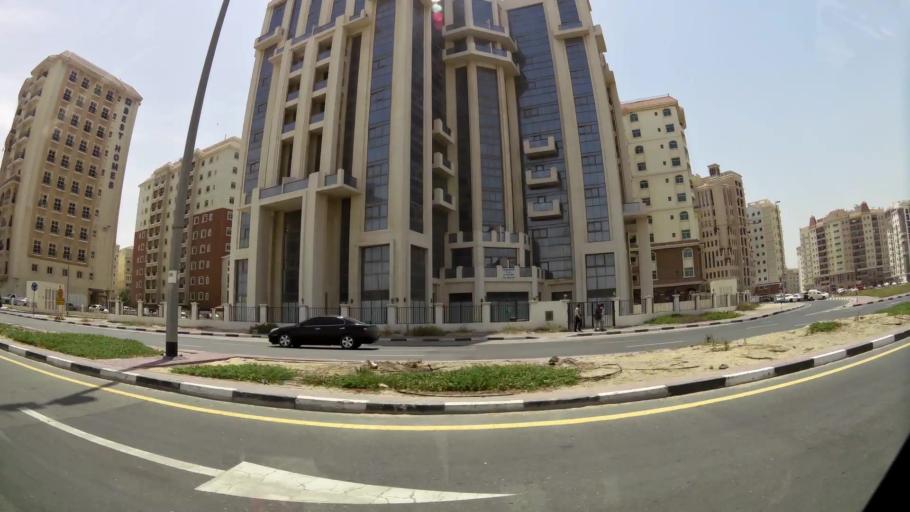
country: AE
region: Ash Shariqah
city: Sharjah
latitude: 25.1645
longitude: 55.4078
